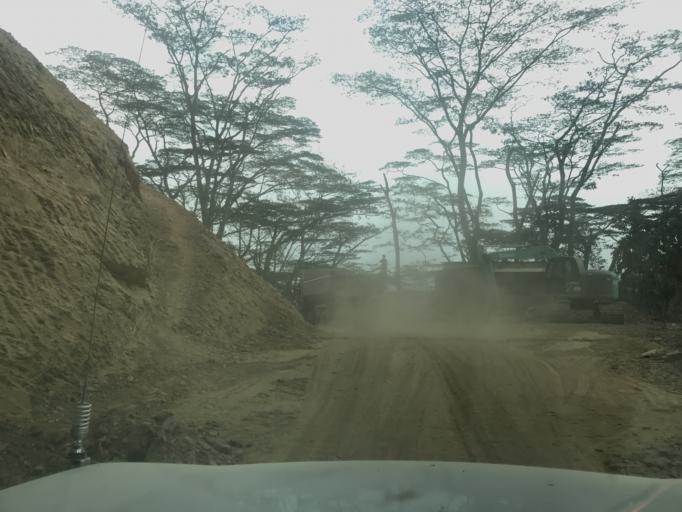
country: TL
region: Ermera
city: Gleno
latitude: -8.7636
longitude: 125.4327
